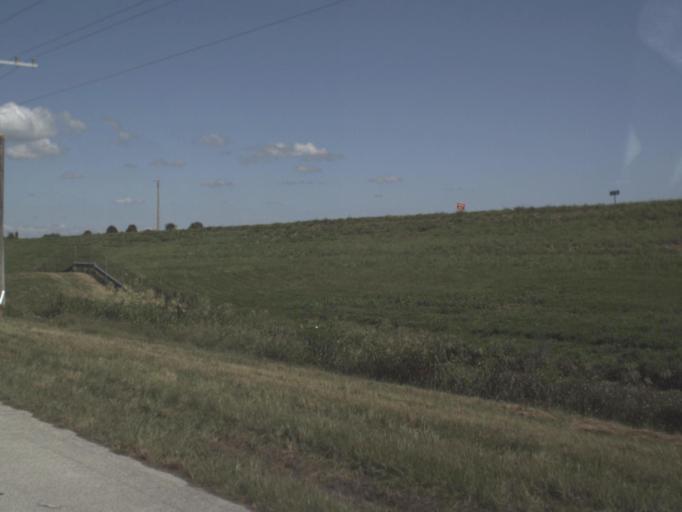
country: US
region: Florida
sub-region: Glades County
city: Moore Haven
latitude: 26.9181
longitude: -81.1223
